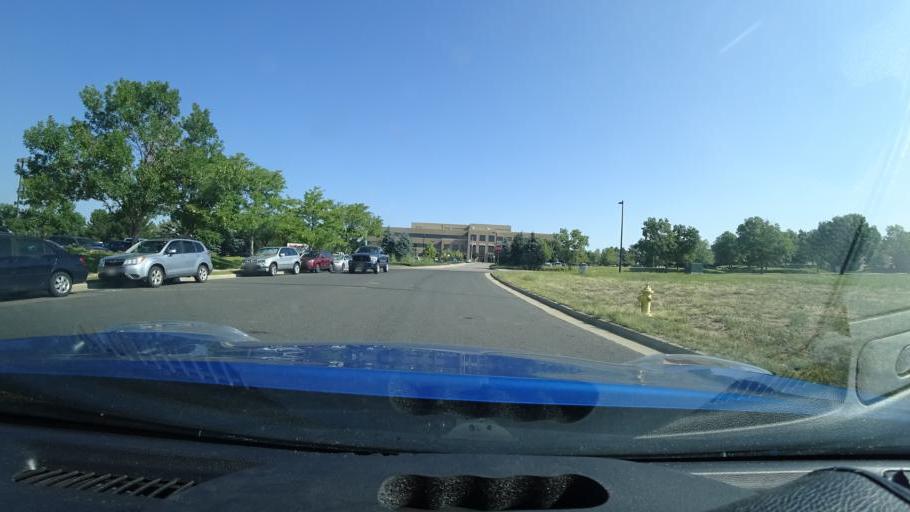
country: US
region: Colorado
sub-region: Adams County
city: Aurora
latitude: 39.7162
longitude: -104.7967
